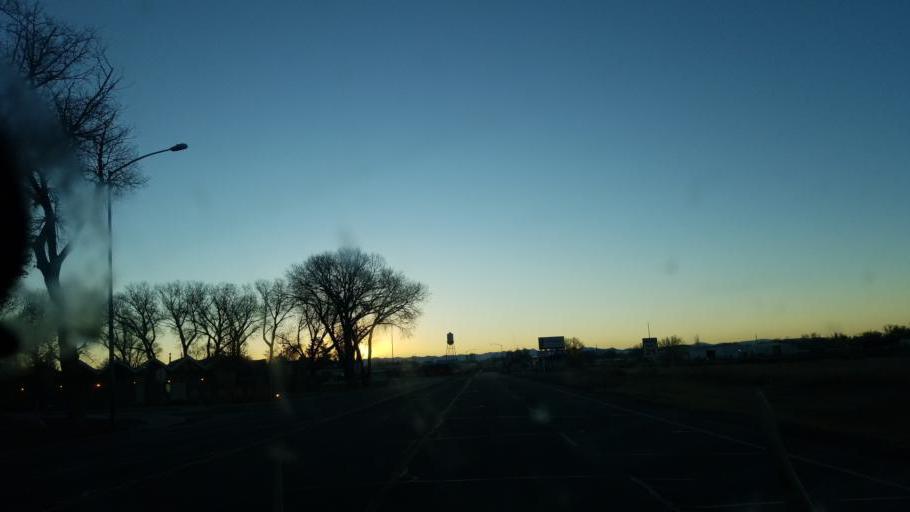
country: US
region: Colorado
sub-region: Alamosa County
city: Alamosa
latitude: 37.4690
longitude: -105.8803
